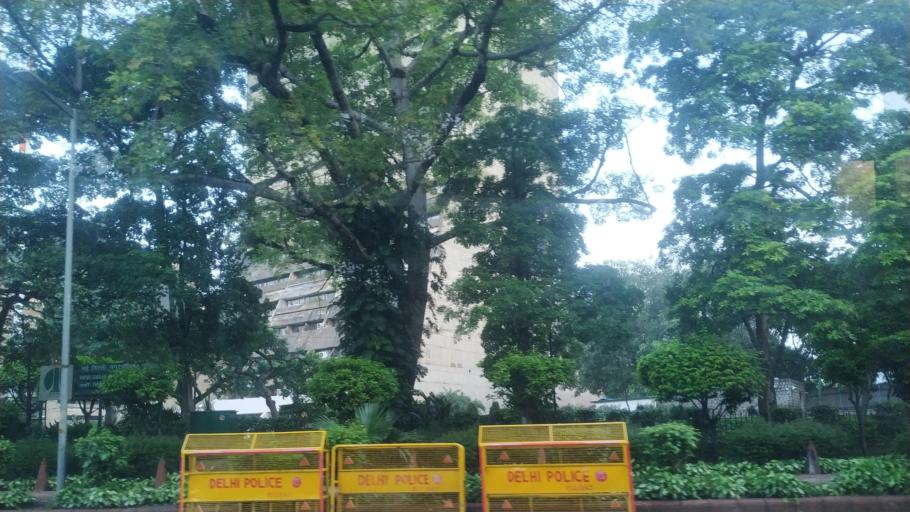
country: IN
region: NCT
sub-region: New Delhi
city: New Delhi
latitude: 28.6282
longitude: 77.2162
